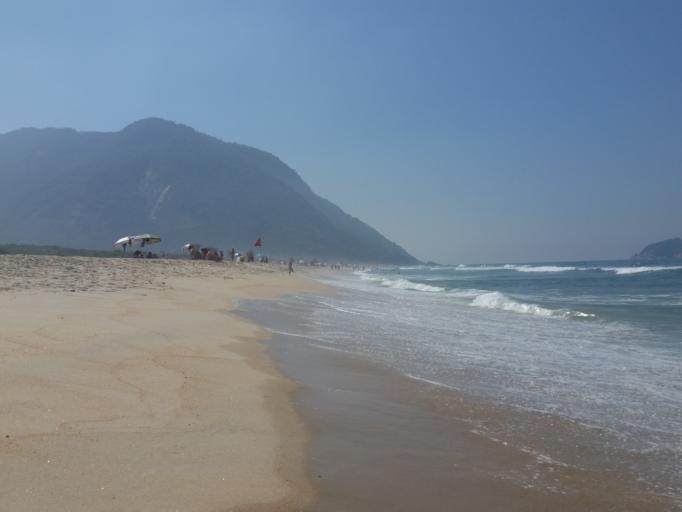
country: BR
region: Rio de Janeiro
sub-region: Nilopolis
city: Nilopolis
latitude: -23.0493
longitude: -43.5285
